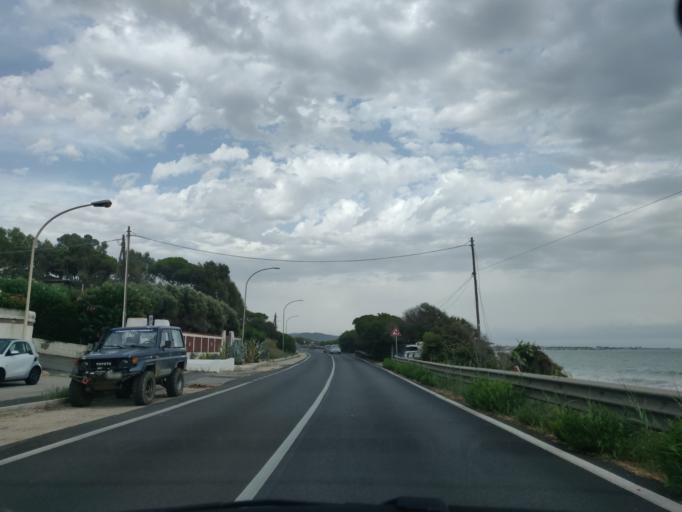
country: IT
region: Latium
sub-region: Citta metropolitana di Roma Capitale
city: Santa Marinella
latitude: 42.0391
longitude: 11.8986
